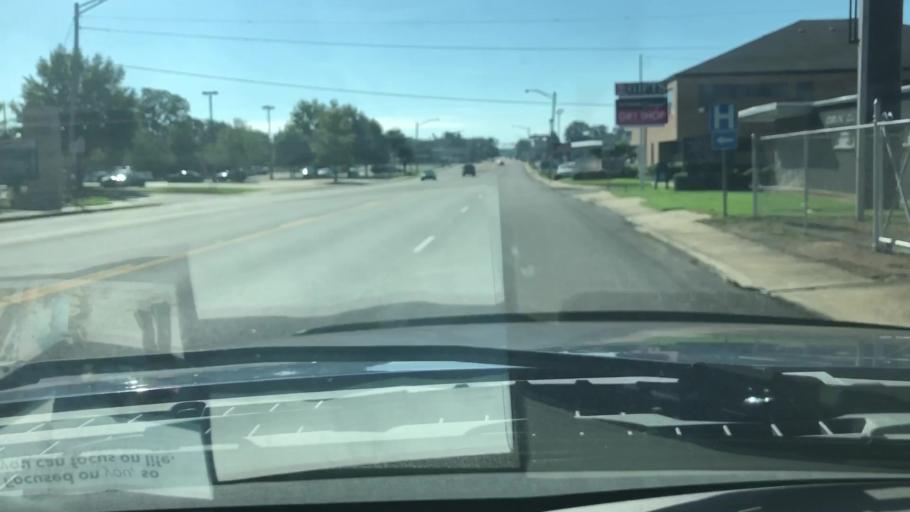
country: US
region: Texas
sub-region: Bowie County
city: Texarkana
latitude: 33.4282
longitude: -94.0500
